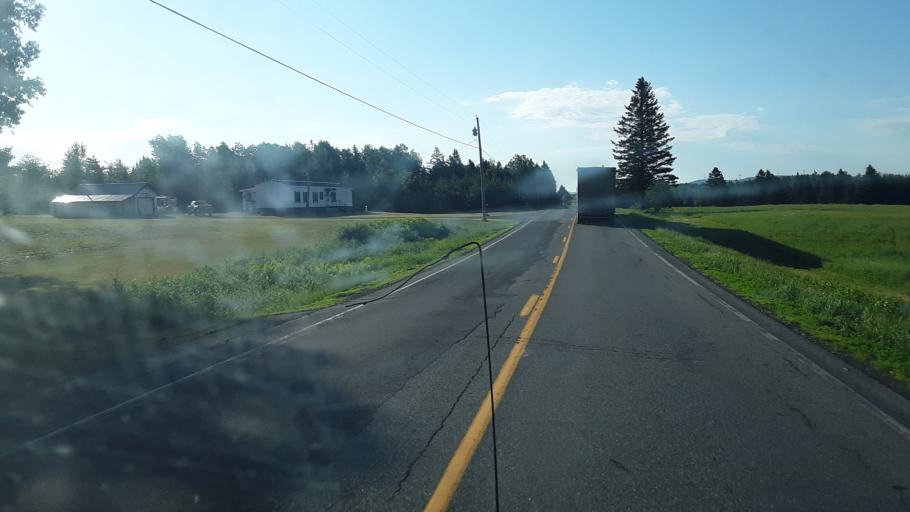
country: US
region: Maine
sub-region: Penobscot County
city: Patten
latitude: 46.1418
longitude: -68.2035
